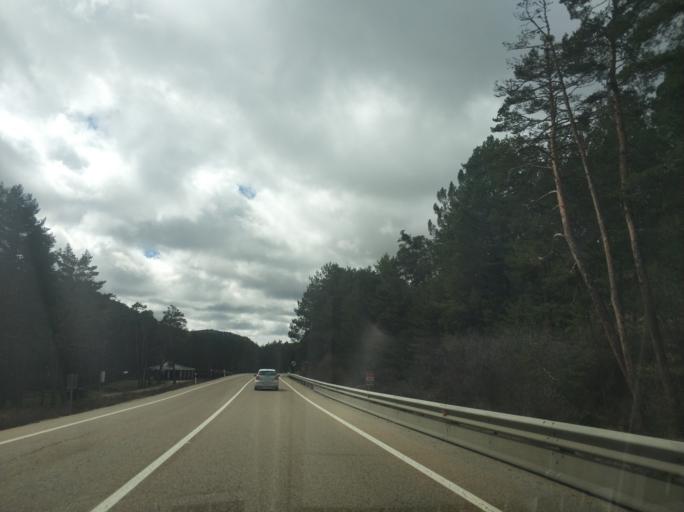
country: ES
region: Castille and Leon
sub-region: Provincia de Soria
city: San Leonardo de Yague
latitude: 41.8355
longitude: -3.0448
